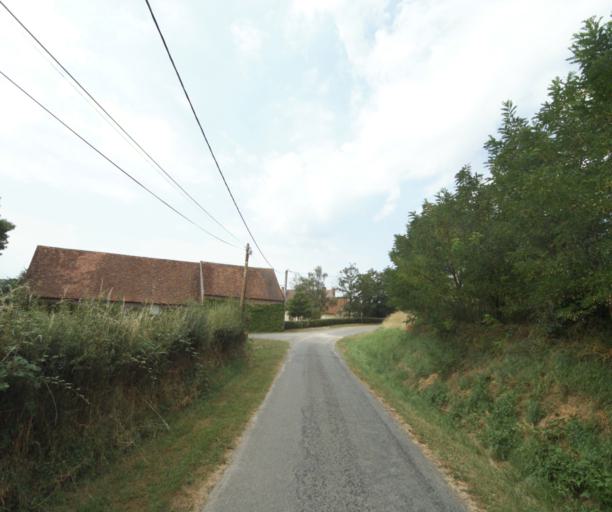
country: FR
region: Bourgogne
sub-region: Departement de Saone-et-Loire
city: Gueugnon
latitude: 46.5797
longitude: 4.0391
